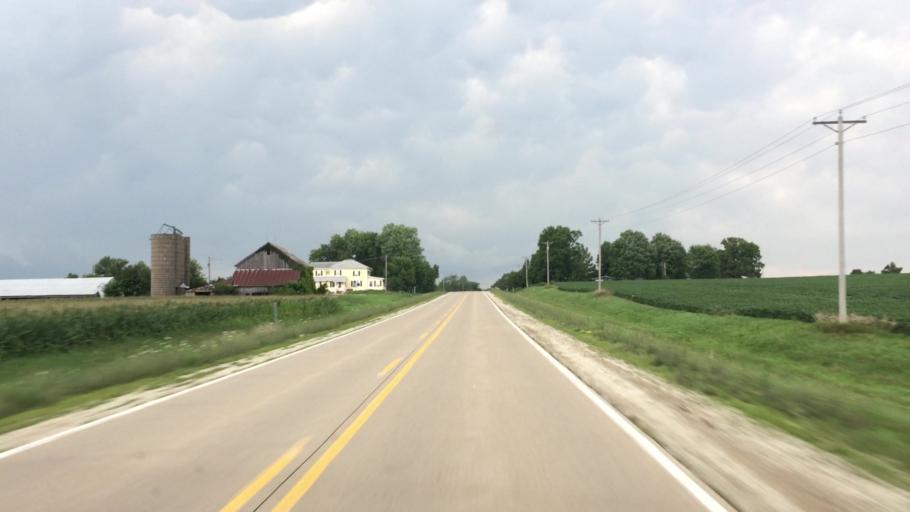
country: US
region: Iowa
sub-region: Lee County
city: Fort Madison
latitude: 40.7277
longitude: -91.3296
